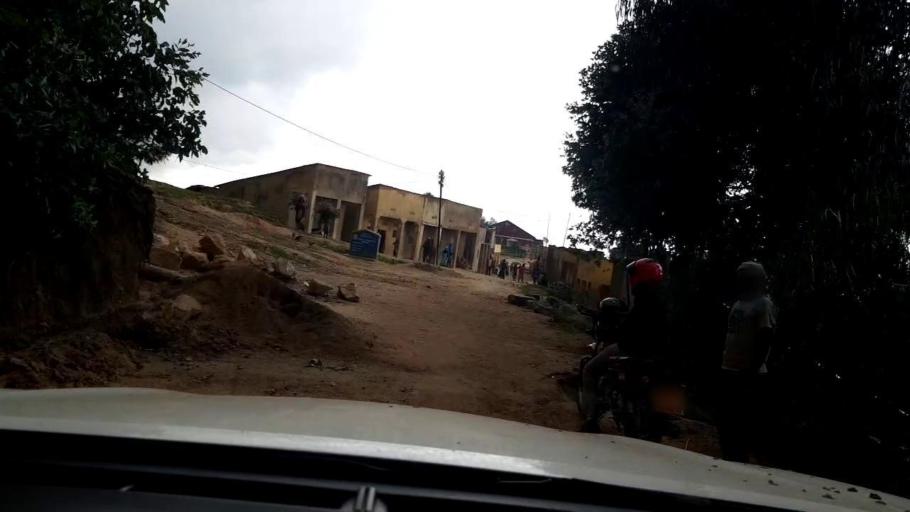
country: RW
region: Western Province
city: Kibuye
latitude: -1.8954
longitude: 29.5320
